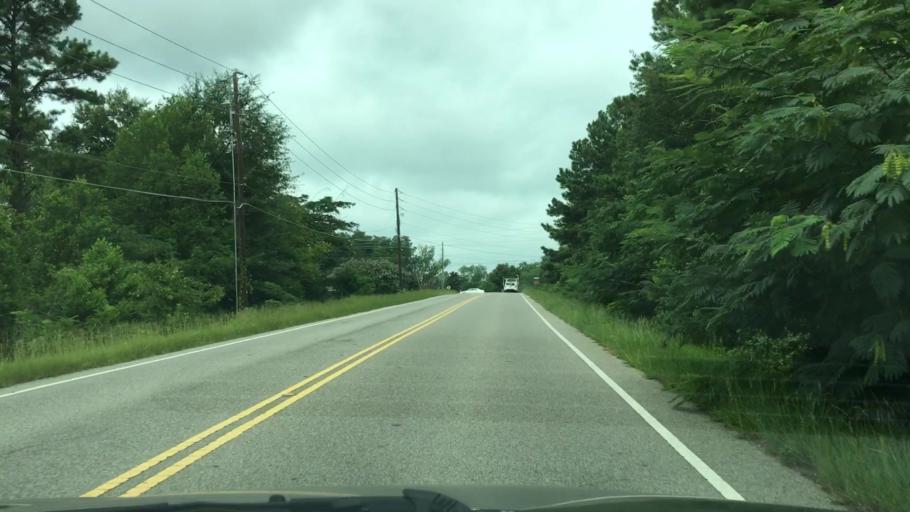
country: US
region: South Carolina
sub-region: Aiken County
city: Belvedere
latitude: 33.5510
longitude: -81.9554
